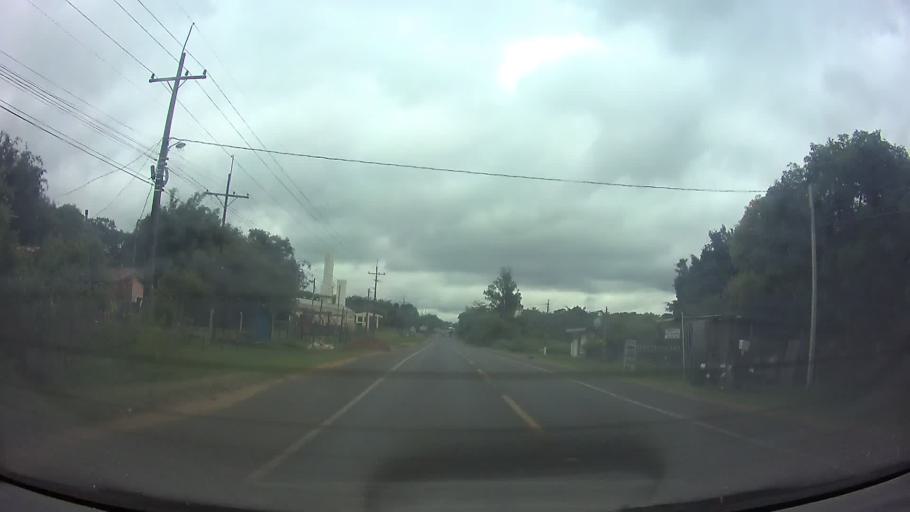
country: PY
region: Central
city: Guarambare
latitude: -25.4991
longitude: -57.4834
